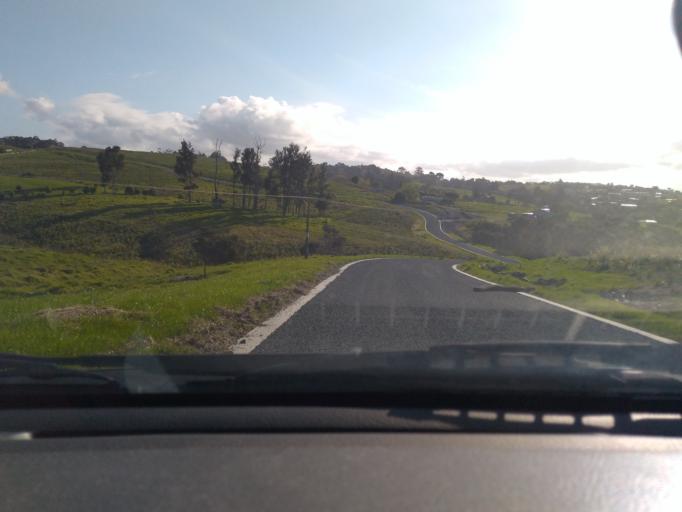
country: NZ
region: Auckland
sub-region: Auckland
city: Warkworth
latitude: -36.4391
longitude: 174.7554
